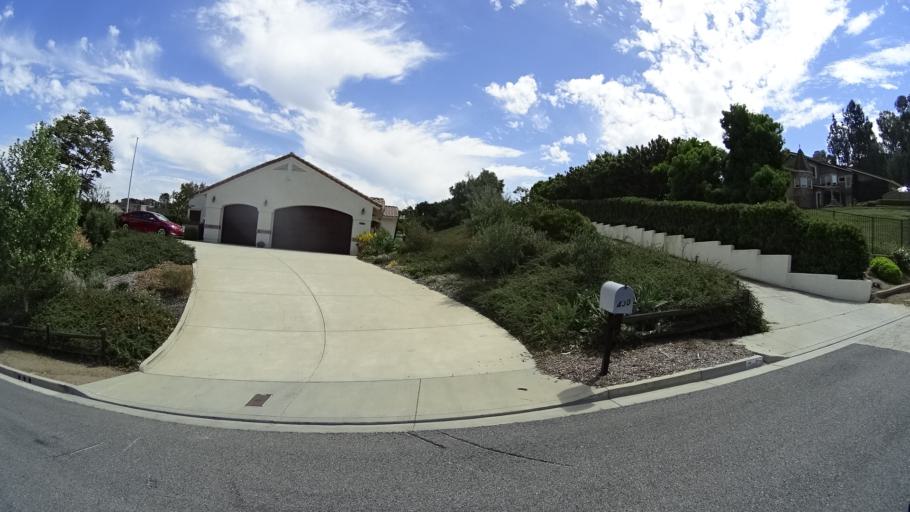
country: US
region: California
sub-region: Ventura County
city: Casa Conejo
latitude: 34.1703
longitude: -118.9331
